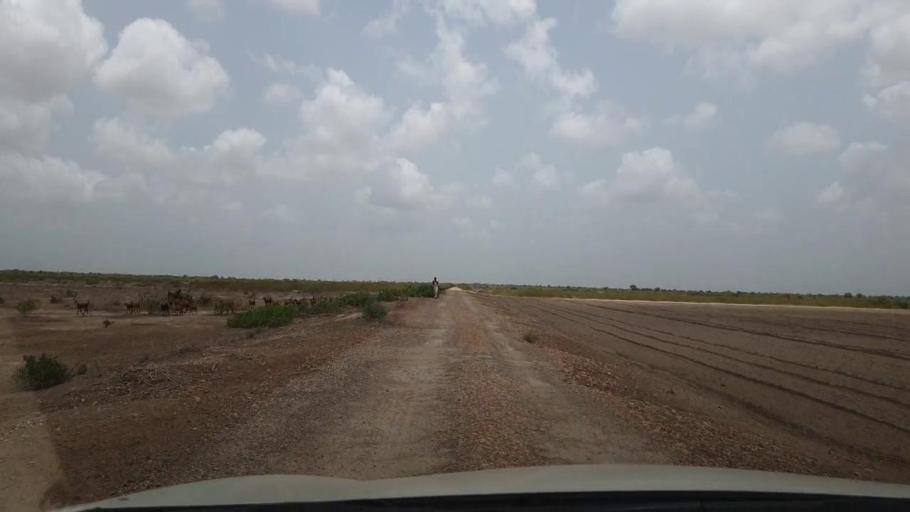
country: PK
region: Sindh
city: Chambar
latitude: 25.2276
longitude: 68.7596
